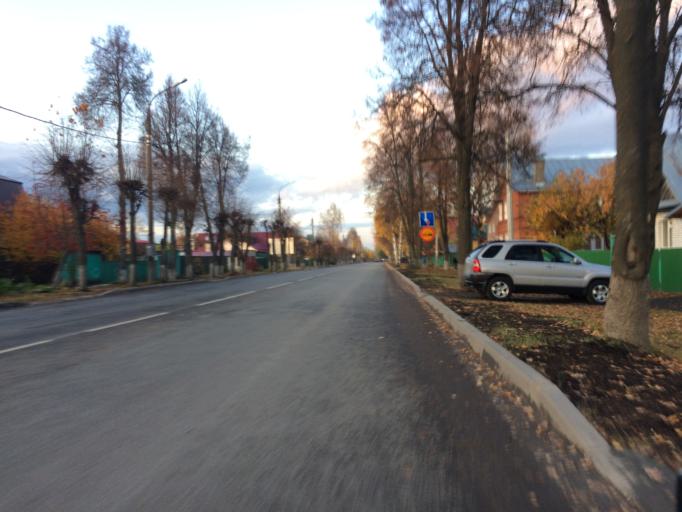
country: RU
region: Mariy-El
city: Yoshkar-Ola
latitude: 56.6504
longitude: 47.8951
